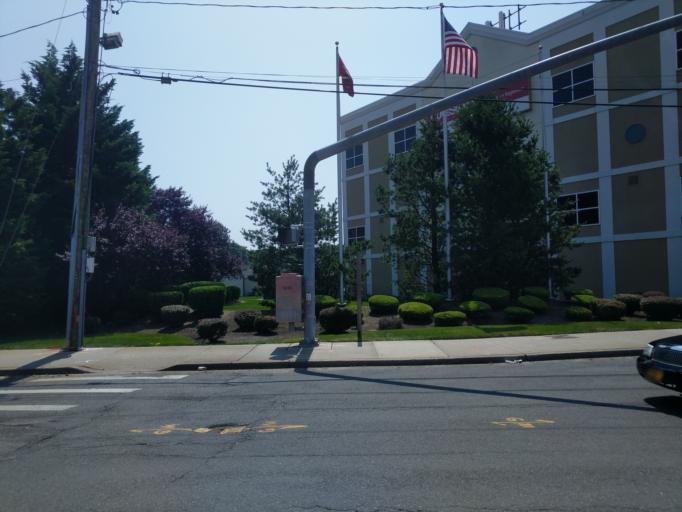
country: US
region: New York
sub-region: Nassau County
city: West Hempstead
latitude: 40.7023
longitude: -73.6432
